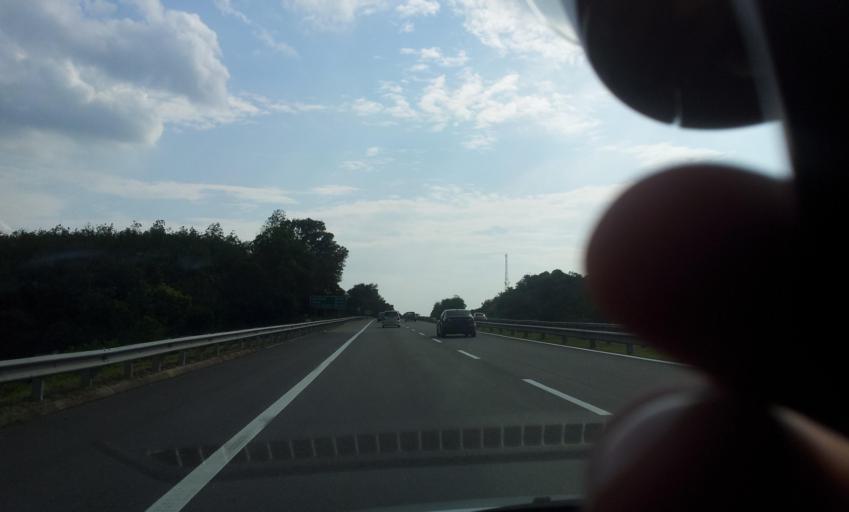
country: MY
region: Pahang
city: Mentekab
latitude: 3.5051
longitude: 102.3887
